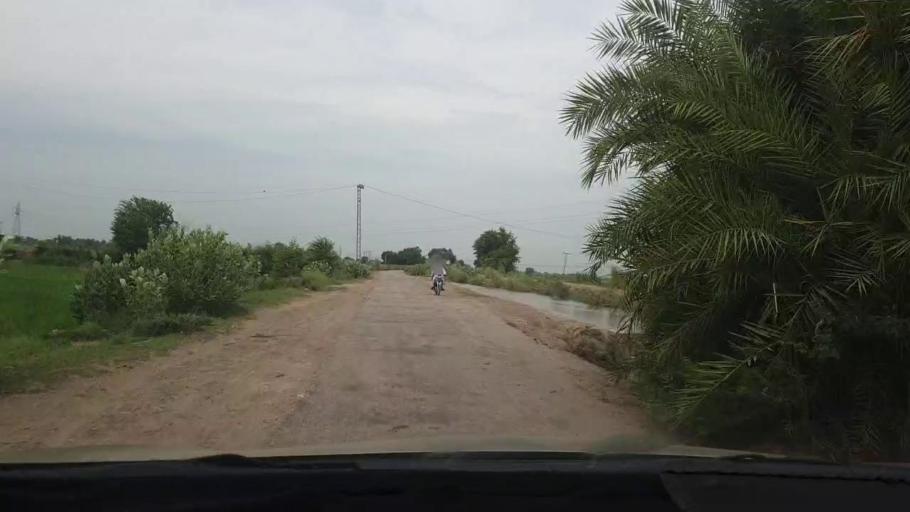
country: PK
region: Sindh
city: Naudero
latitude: 27.6792
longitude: 68.3473
